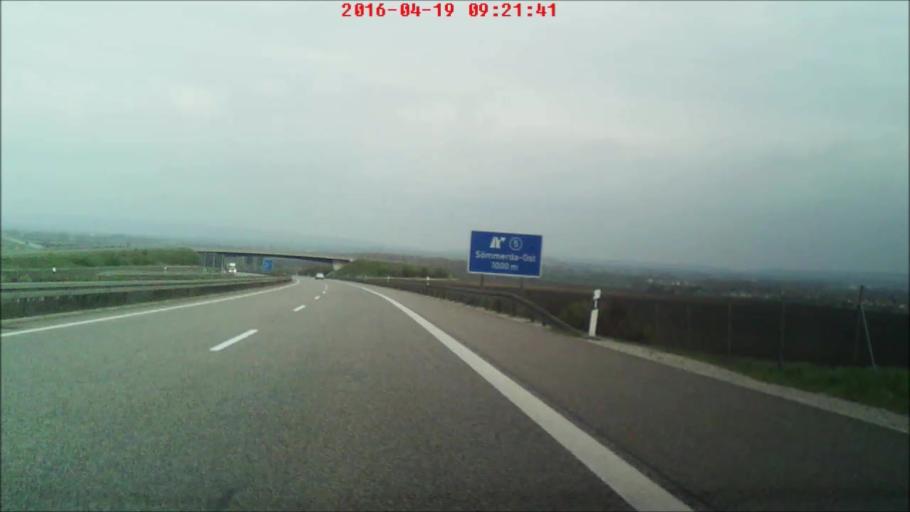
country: DE
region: Thuringia
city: Sprotau
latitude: 51.1421
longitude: 11.1749
